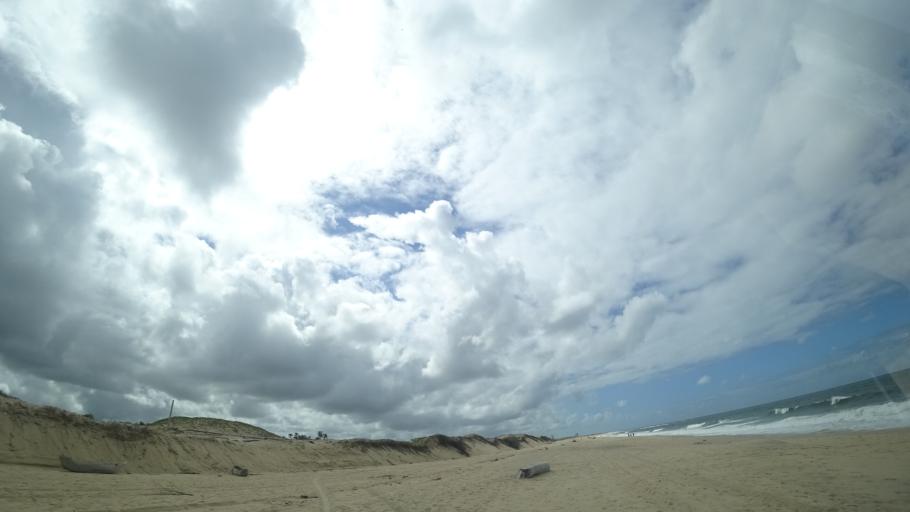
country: MZ
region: Sofala
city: Beira
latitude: -19.6148
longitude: 35.2215
